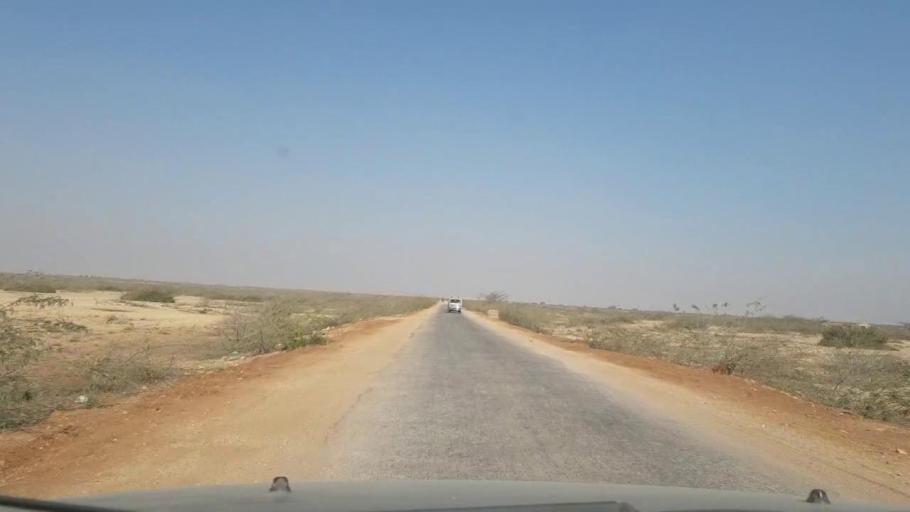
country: PK
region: Sindh
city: Thatta
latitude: 24.9392
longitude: 67.9507
